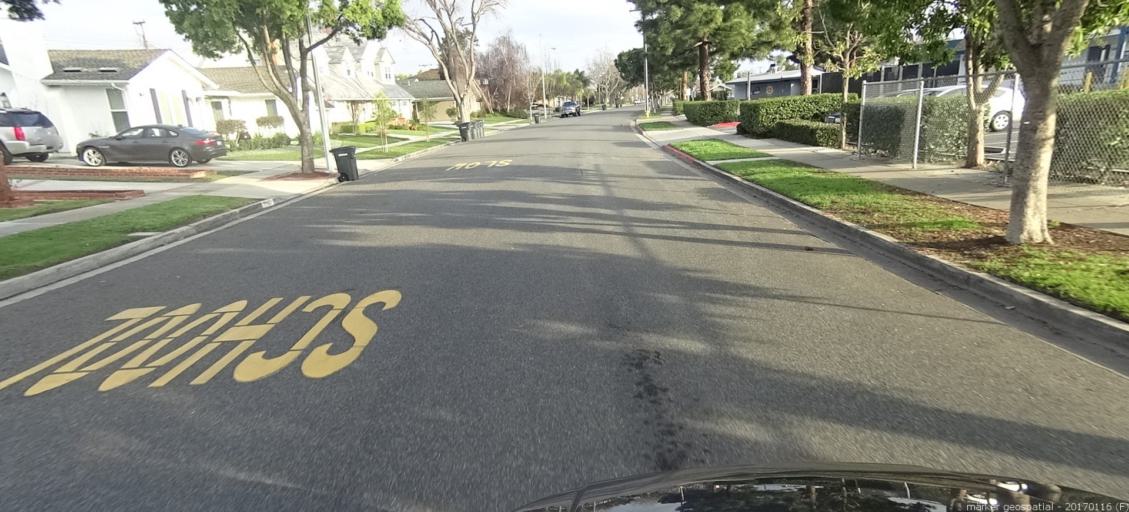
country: US
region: California
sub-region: Orange County
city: Rossmoor
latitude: 33.7893
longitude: -118.0862
